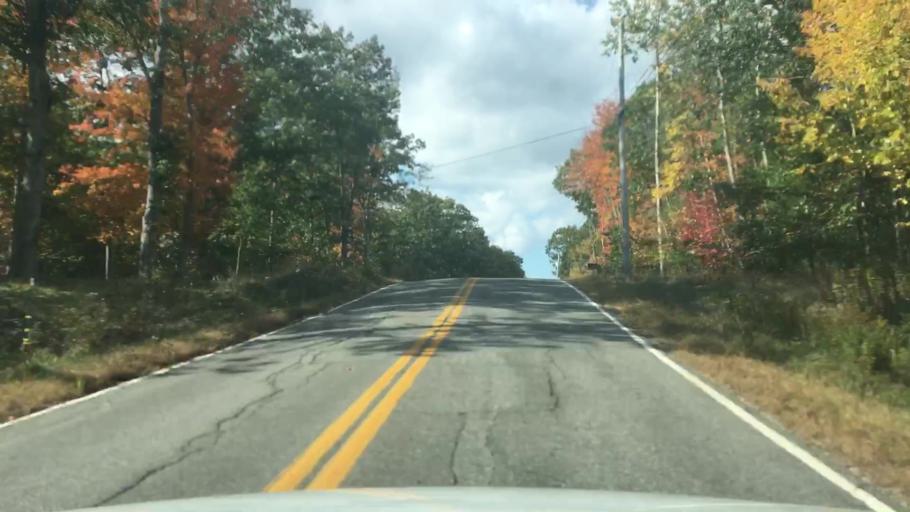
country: US
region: Maine
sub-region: Knox County
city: Washington
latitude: 44.2994
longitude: -69.3196
